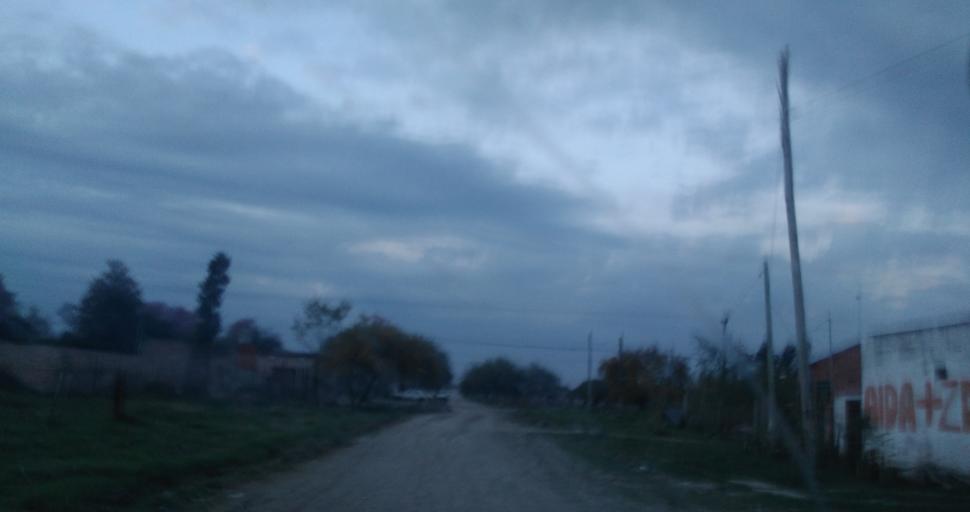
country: AR
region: Chaco
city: Resistencia
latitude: -27.4811
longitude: -59.0022
